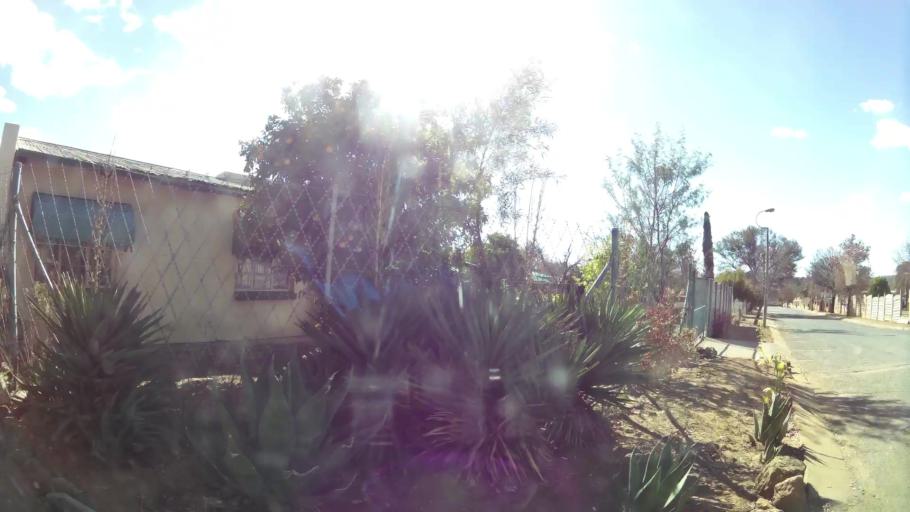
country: ZA
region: North-West
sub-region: Dr Kenneth Kaunda District Municipality
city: Klerksdorp
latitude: -26.8567
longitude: 26.6503
